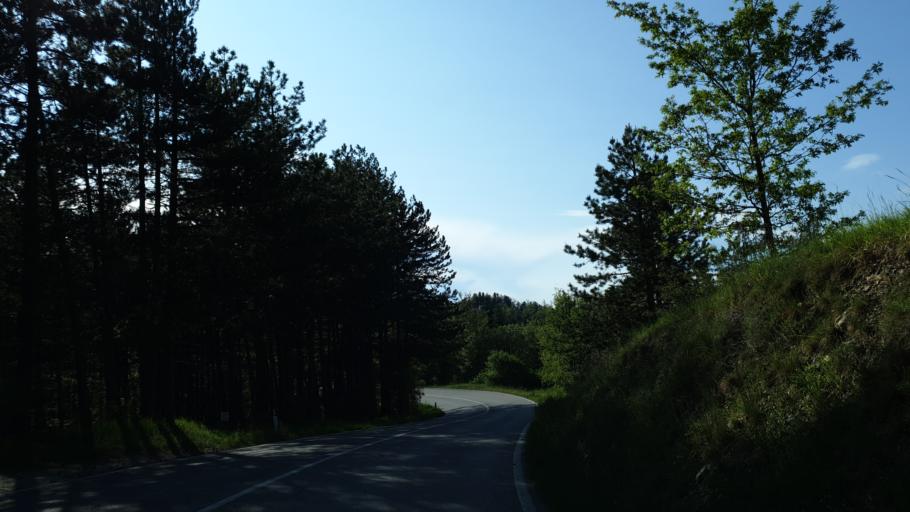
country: IT
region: Tuscany
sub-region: Province of Arezzo
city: Montemignaio
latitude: 43.7879
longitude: 11.6349
